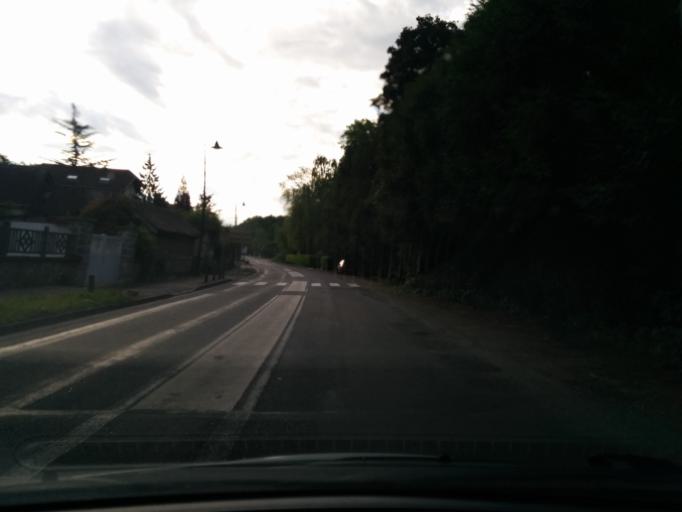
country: FR
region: Ile-de-France
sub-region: Departement des Yvelines
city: Limetz-Villez
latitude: 49.0741
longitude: 1.5385
